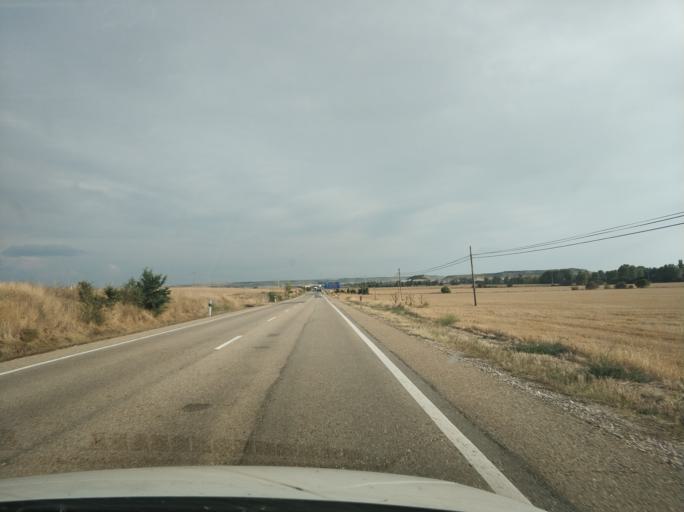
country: ES
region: Castille and Leon
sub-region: Provincia de Burgos
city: Quintanaortuno
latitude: 42.4792
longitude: -3.6929
